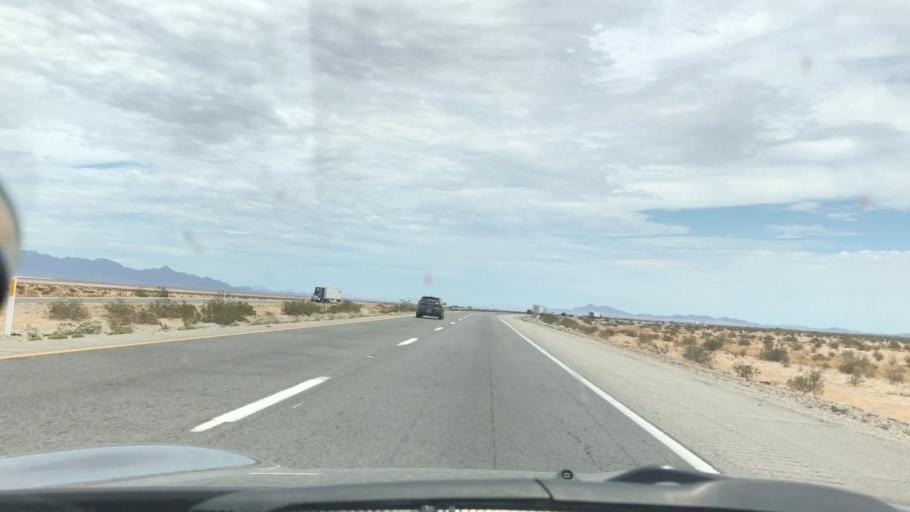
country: US
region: California
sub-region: Riverside County
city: Mesa Verde
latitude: 33.6369
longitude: -115.0855
